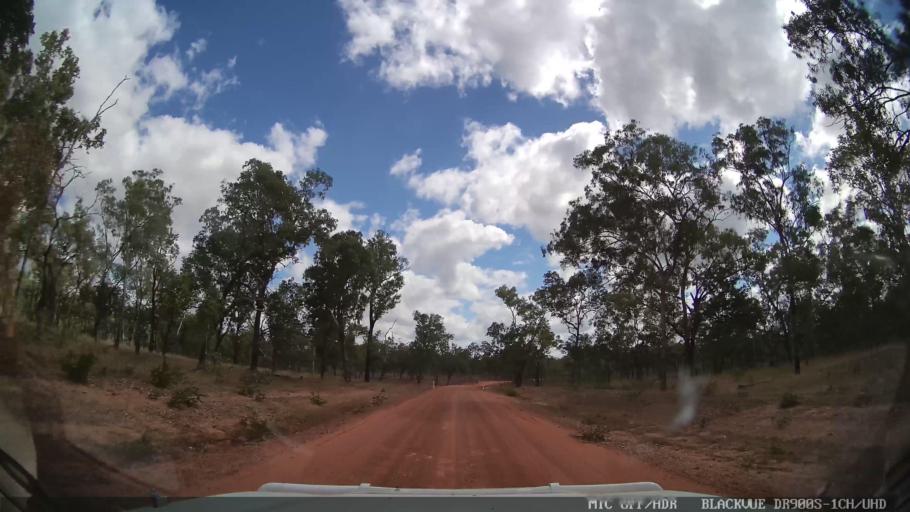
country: AU
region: Queensland
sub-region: Cook
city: Cooktown
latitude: -15.3521
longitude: 144.4616
